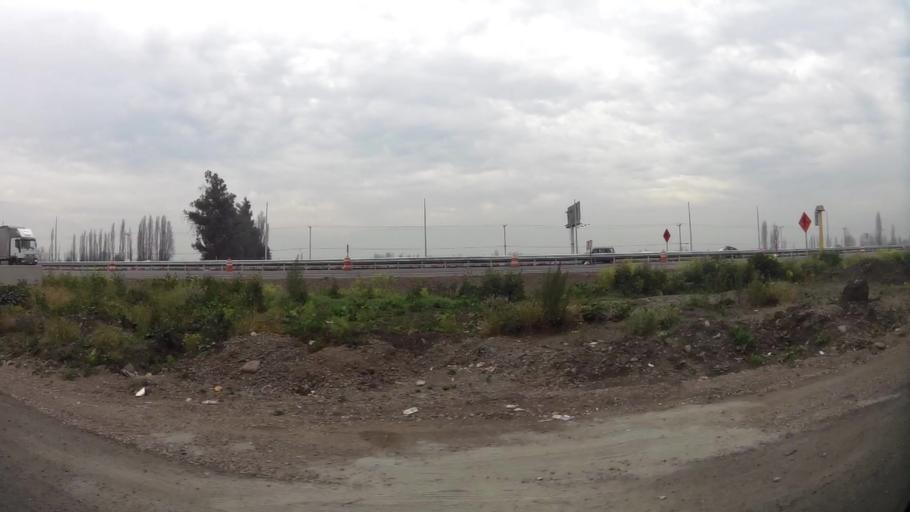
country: CL
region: Santiago Metropolitan
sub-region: Provincia de Chacabuco
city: Chicureo Abajo
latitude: -33.2612
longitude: -70.7479
